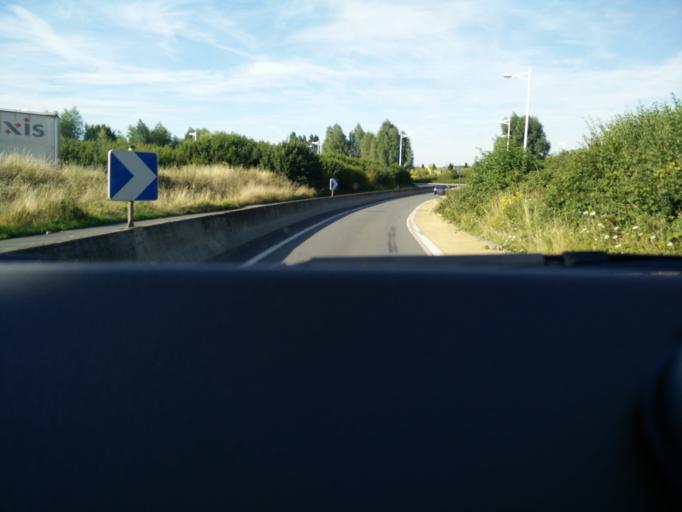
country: FR
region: Nord-Pas-de-Calais
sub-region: Departement du Nord
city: Feignies
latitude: 50.2788
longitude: 3.9220
